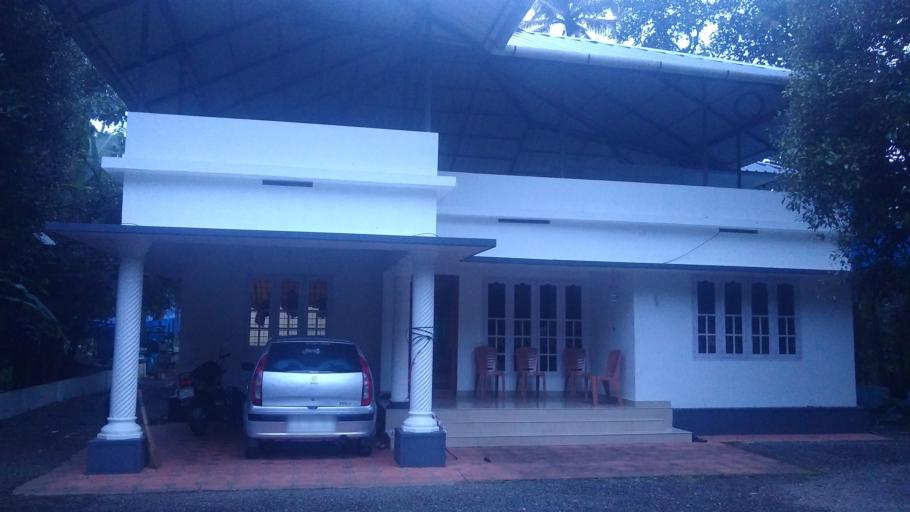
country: IN
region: Kerala
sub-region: Ernakulam
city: Ramamangalam
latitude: 9.9839
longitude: 76.4620
